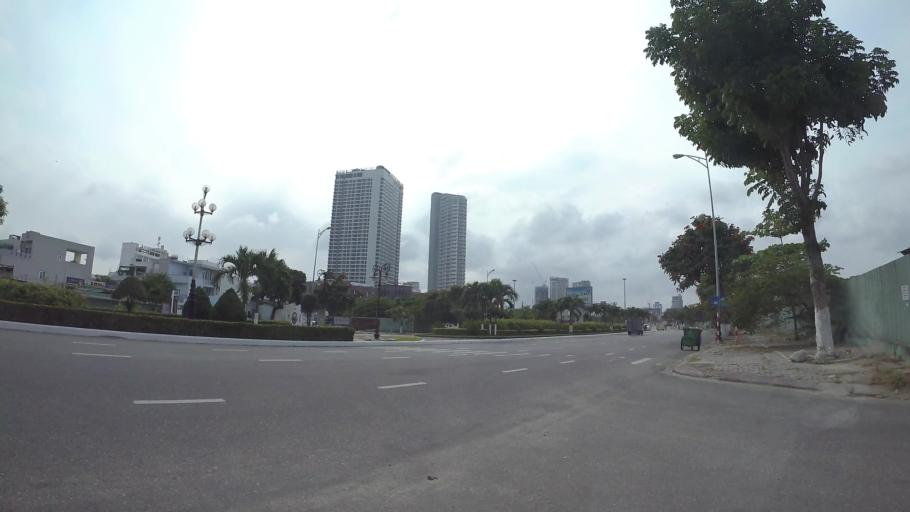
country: VN
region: Da Nang
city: Son Tra
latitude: 16.0725
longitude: 108.2329
